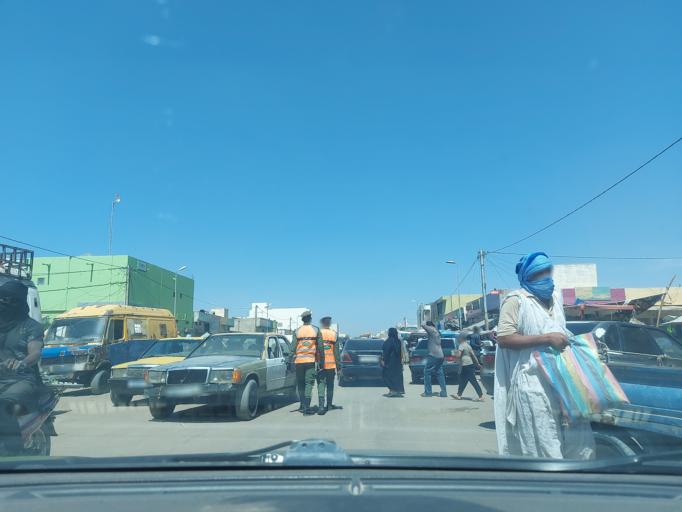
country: MR
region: Nouakchott
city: Nouakchott
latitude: 18.0819
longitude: -15.9789
